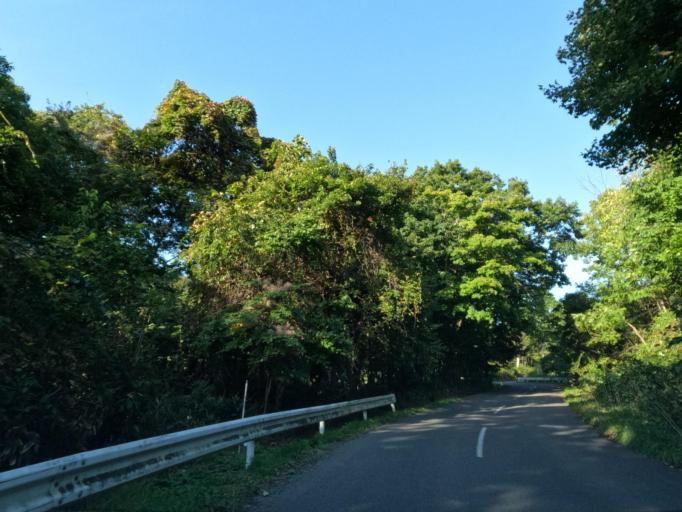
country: JP
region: Hokkaido
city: Date
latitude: 42.4018
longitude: 140.9248
